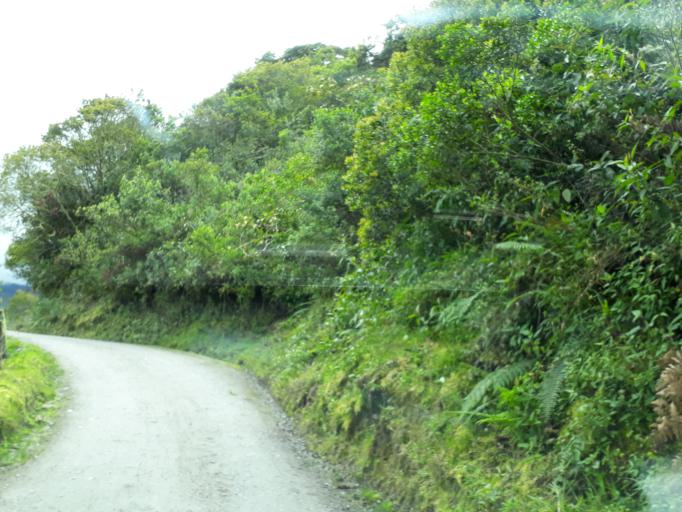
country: CO
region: Cundinamarca
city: Junin
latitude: 4.6847
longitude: -73.6780
